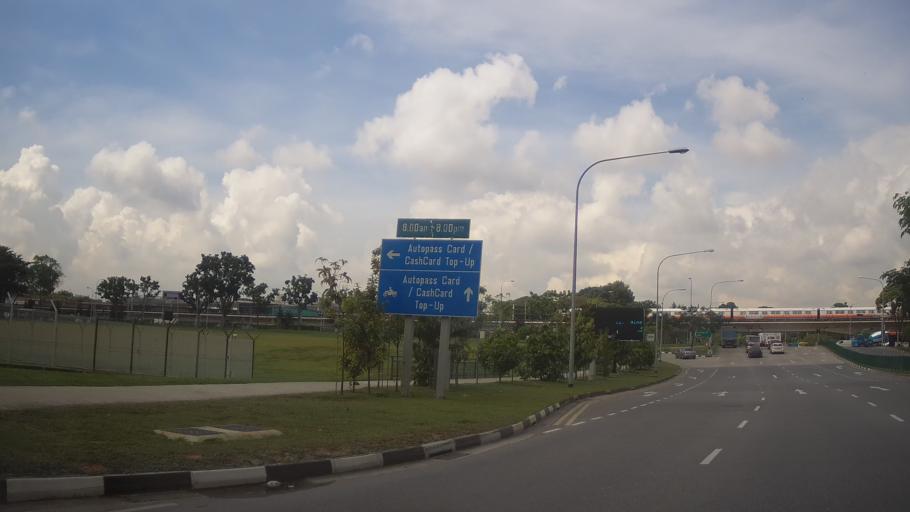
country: MY
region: Johor
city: Johor Bahru
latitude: 1.4249
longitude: 103.7570
